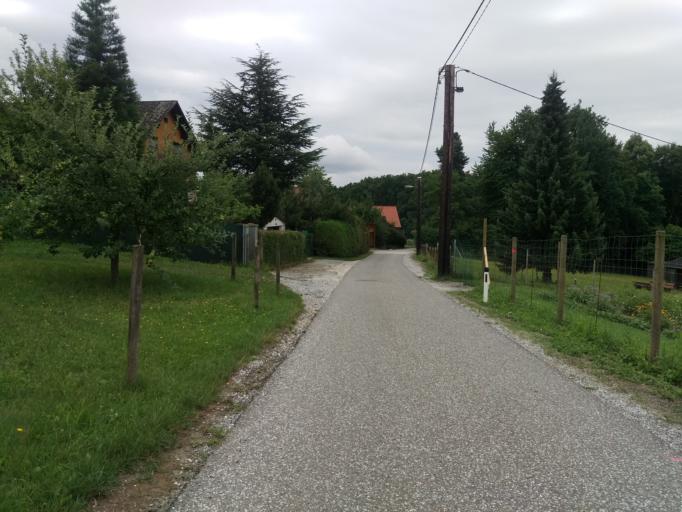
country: AT
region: Styria
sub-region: Politischer Bezirk Graz-Umgebung
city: Raaba
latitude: 47.0503
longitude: 15.4991
